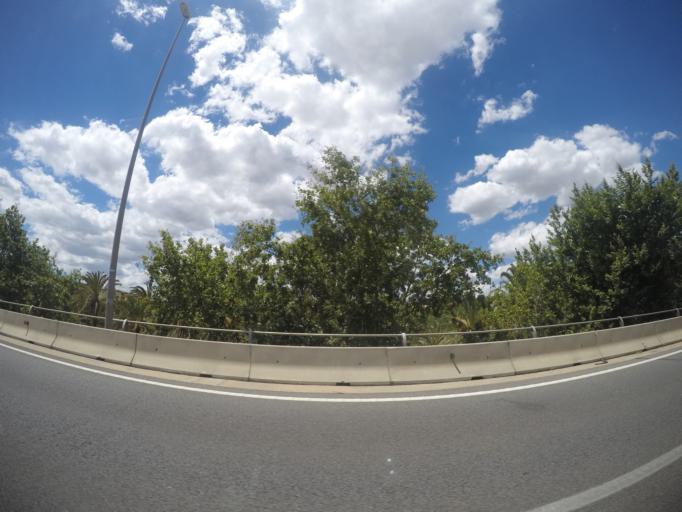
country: ES
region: Catalonia
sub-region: Provincia de Barcelona
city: Llefia
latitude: 41.4351
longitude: 2.2246
